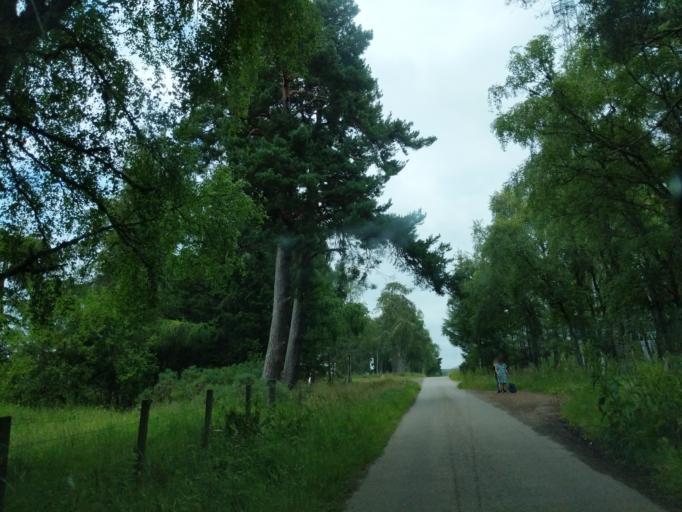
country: GB
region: Scotland
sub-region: Moray
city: Rothes
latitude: 57.4830
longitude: -3.2322
